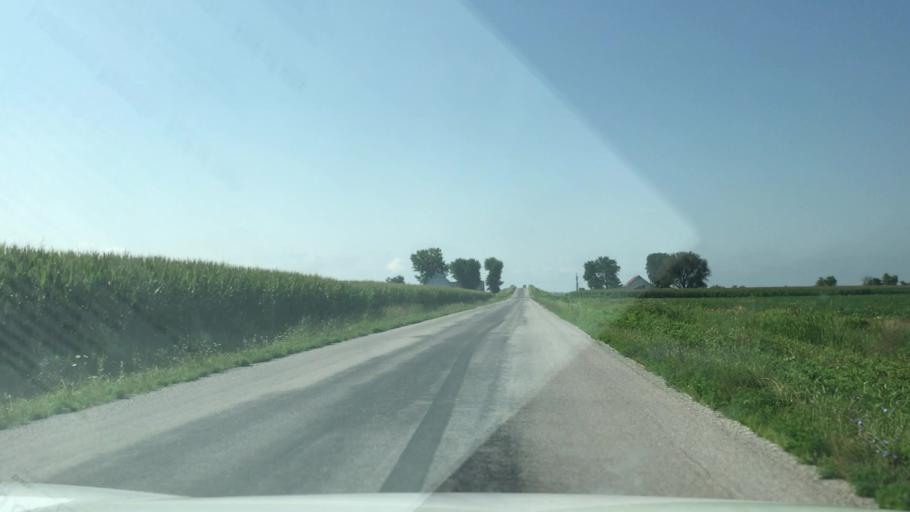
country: US
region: Illinois
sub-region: Washington County
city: Okawville
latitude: 38.4332
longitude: -89.4779
